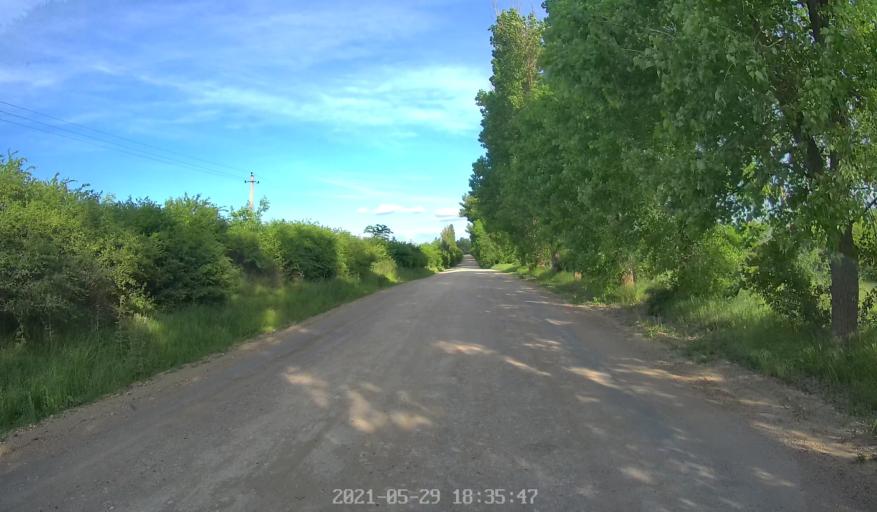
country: MD
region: Chisinau
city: Singera
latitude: 46.8084
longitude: 28.9213
